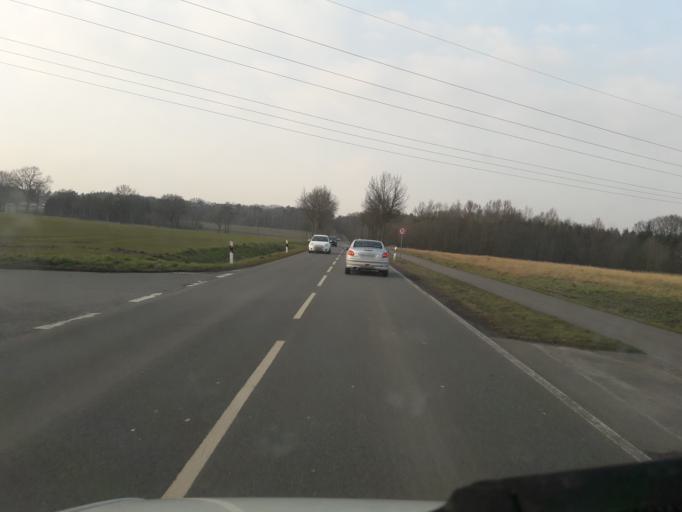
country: DE
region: North Rhine-Westphalia
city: Espelkamp
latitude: 52.3653
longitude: 8.6397
